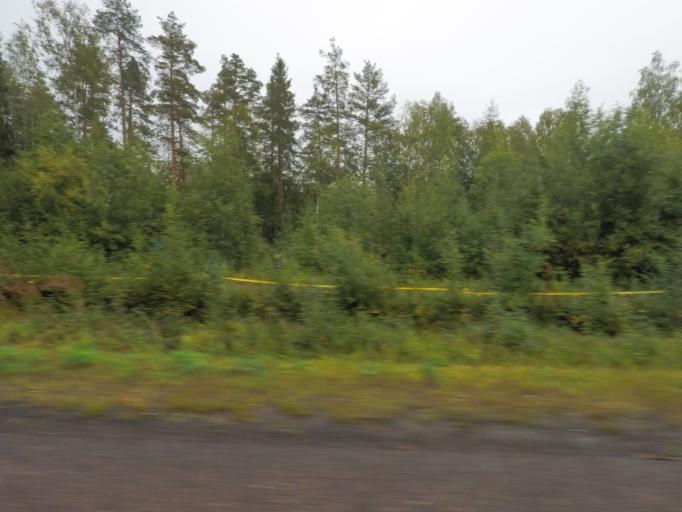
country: FI
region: Northern Savo
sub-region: Varkaus
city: Leppaevirta
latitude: 62.4214
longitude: 27.8186
